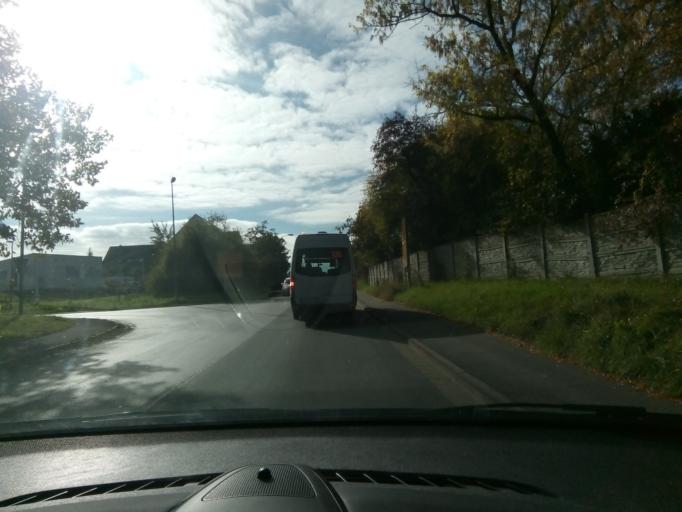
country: DE
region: Bavaria
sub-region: Regierungsbezirk Unterfranken
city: Gerolzhofen
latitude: 49.8956
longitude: 10.3524
